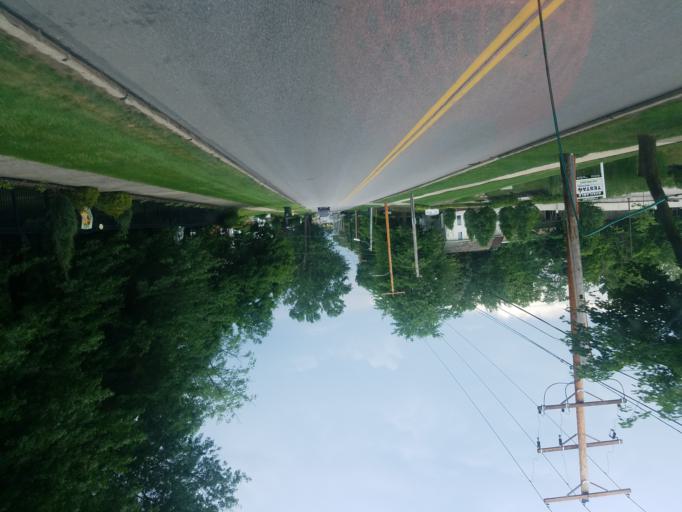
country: US
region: Ohio
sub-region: Medina County
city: Wadsworth
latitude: 41.0319
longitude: -81.7297
